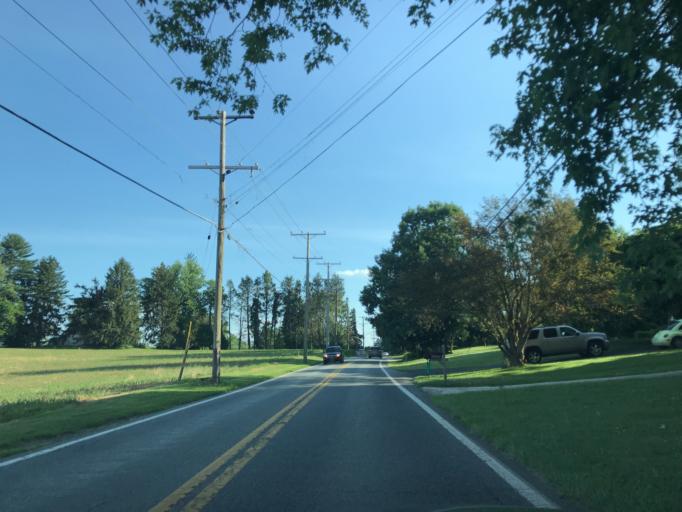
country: US
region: Maryland
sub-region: Baltimore County
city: Carney
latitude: 39.4675
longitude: -76.5261
